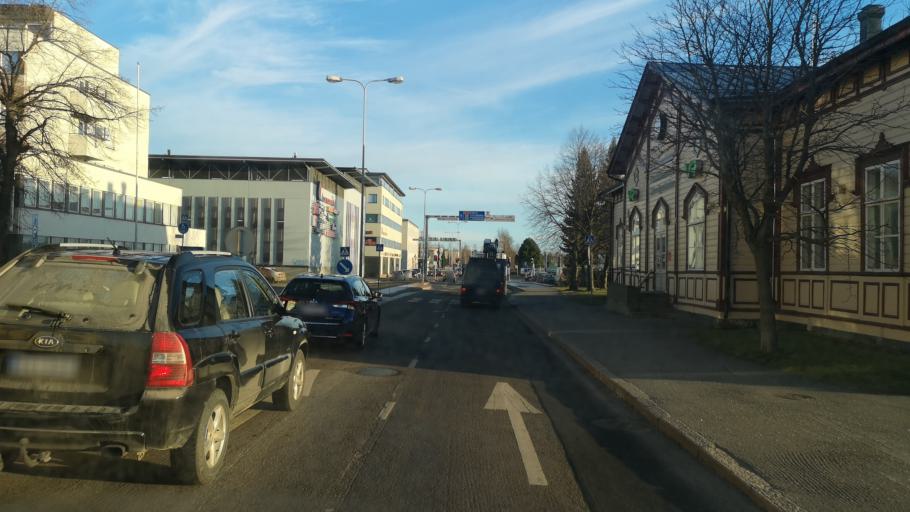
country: FI
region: Central Ostrobothnia
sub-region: Kokkola
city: Kokkola
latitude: 63.8350
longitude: 23.1309
